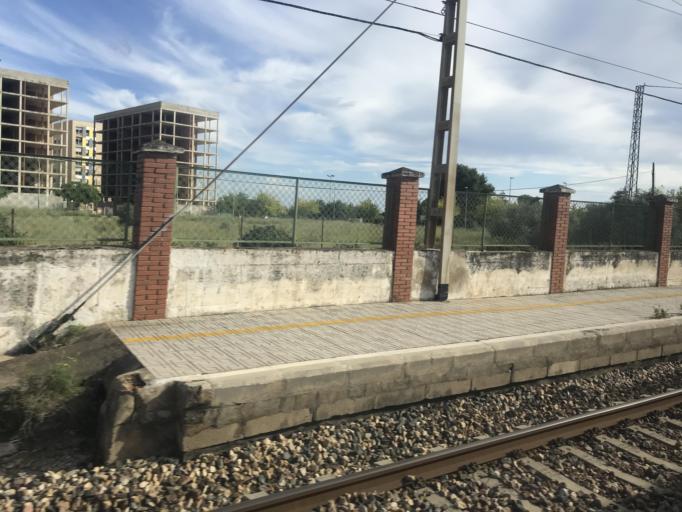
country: ES
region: Valencia
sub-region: Provincia de Castello
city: Vinaros
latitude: 40.4733
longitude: 0.4569
